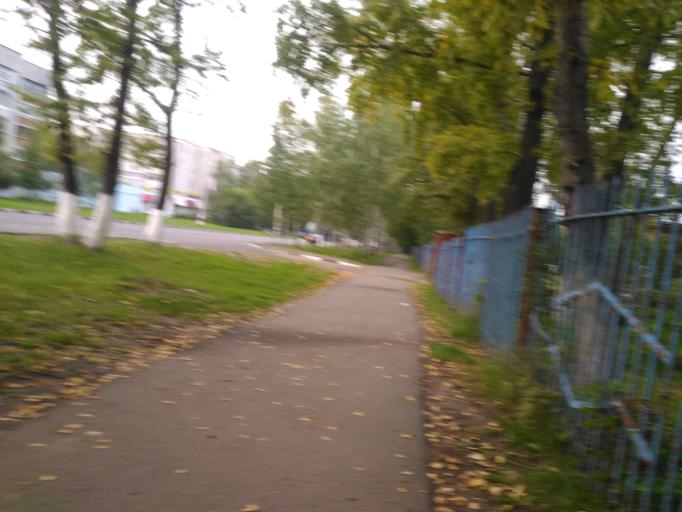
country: RU
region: Ulyanovsk
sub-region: Ulyanovskiy Rayon
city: Ulyanovsk
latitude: 54.2673
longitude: 48.3349
